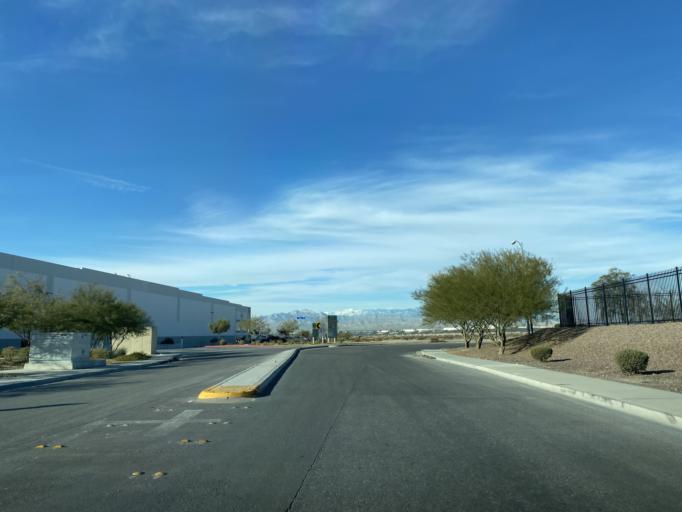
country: US
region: Nevada
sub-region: Clark County
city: Nellis Air Force Base
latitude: 36.2623
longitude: -115.0473
